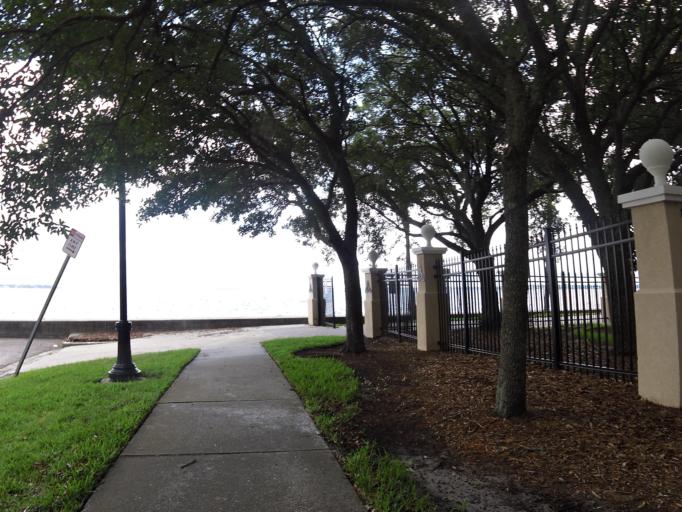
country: US
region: Florida
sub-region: Duval County
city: Jacksonville
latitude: 30.3082
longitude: -81.6873
